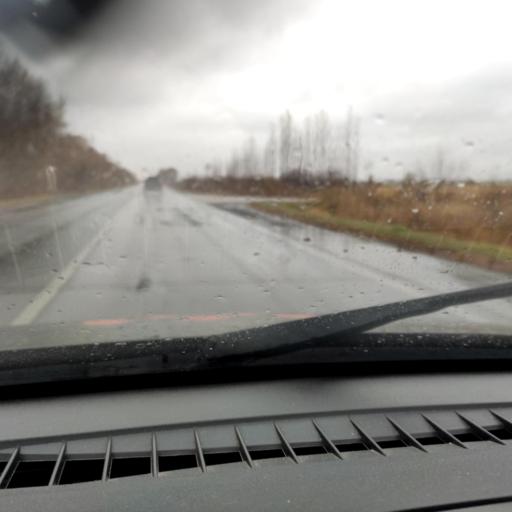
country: RU
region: Samara
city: Tol'yatti
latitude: 53.6181
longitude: 49.3113
